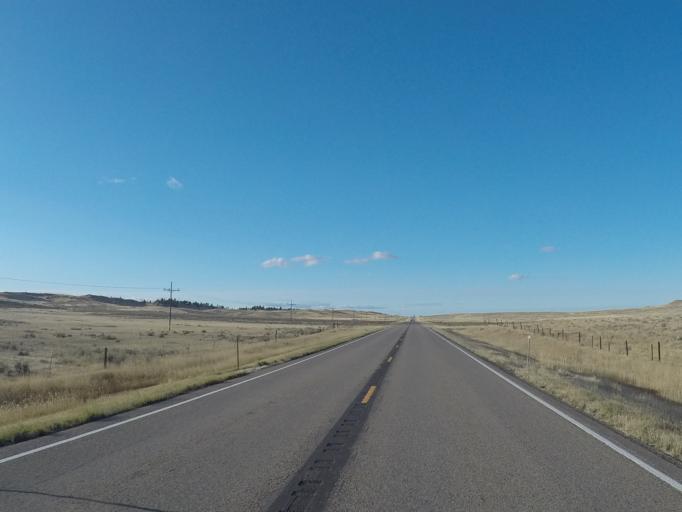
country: US
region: Montana
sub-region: Golden Valley County
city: Ryegate
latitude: 46.2259
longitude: -108.9297
